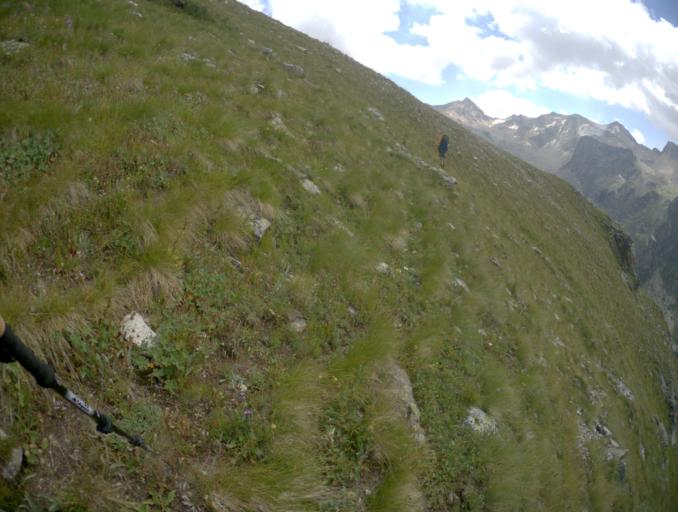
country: RU
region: Karachayevo-Cherkesiya
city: Uchkulan
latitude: 43.2961
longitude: 42.0709
